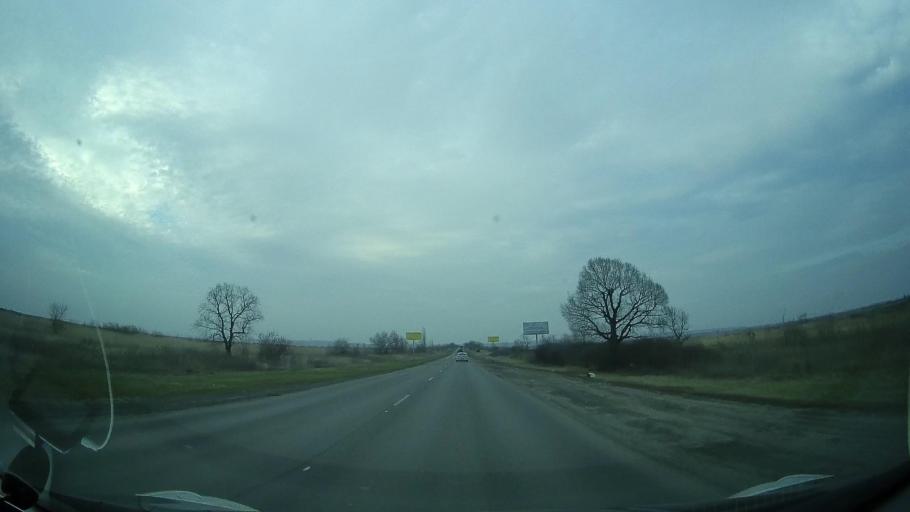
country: RU
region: Rostov
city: Ol'ginskaya
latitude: 47.2017
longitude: 39.9317
